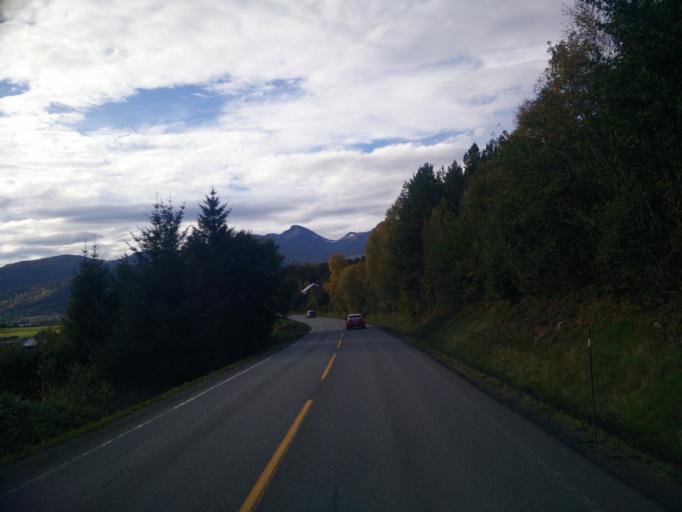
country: NO
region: More og Romsdal
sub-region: Vestnes
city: Vestnes
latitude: 62.6393
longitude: 7.0784
